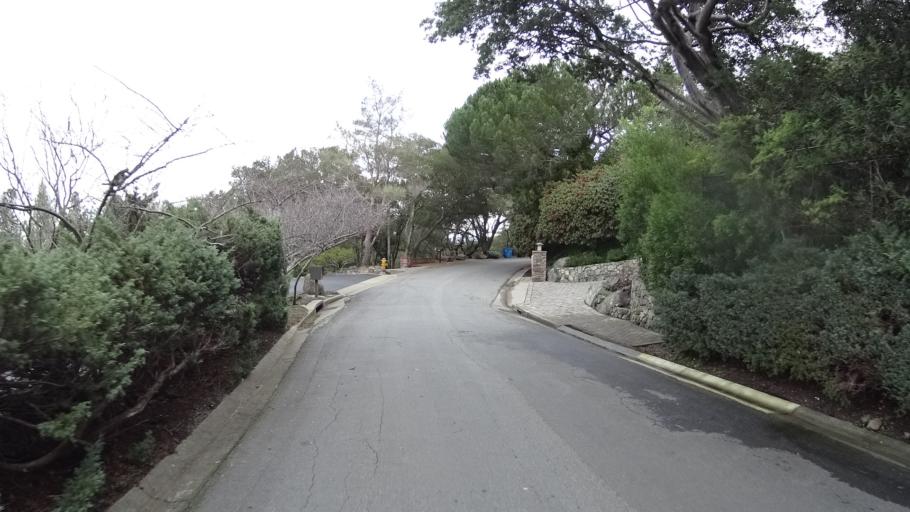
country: US
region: California
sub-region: San Mateo County
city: Hillsborough
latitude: 37.5591
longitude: -122.3716
